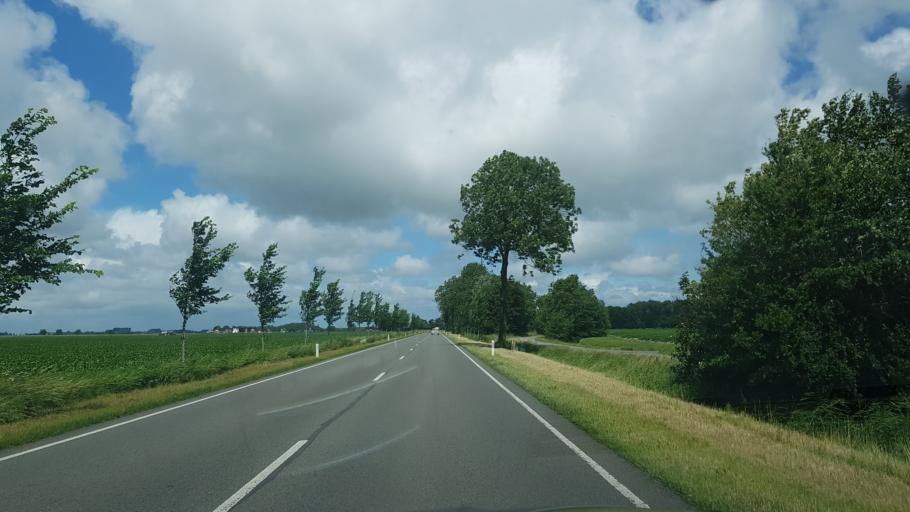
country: NL
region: Groningen
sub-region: Gemeente Winsum
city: Winsum
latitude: 53.3539
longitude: 6.5071
